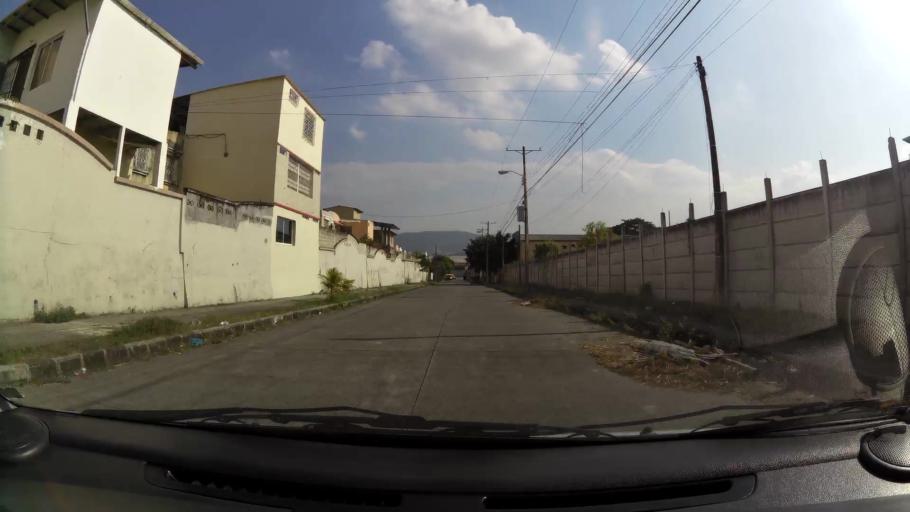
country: EC
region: Guayas
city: Guayaquil
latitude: -2.1324
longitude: -79.9279
